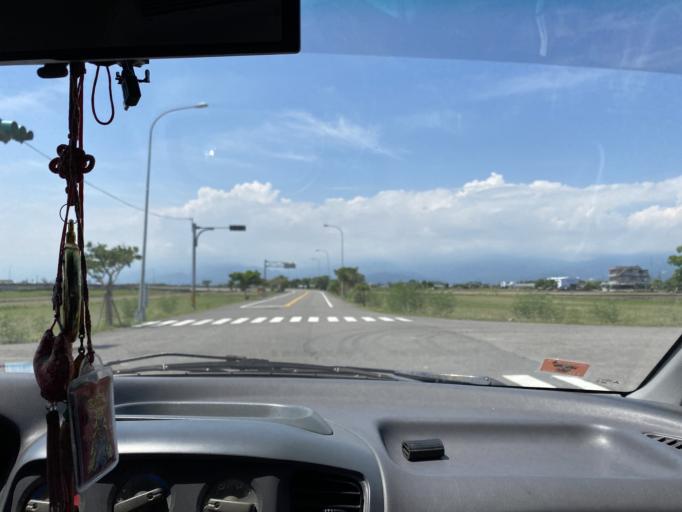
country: TW
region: Taiwan
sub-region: Yilan
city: Yilan
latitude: 24.7246
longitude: 121.8120
